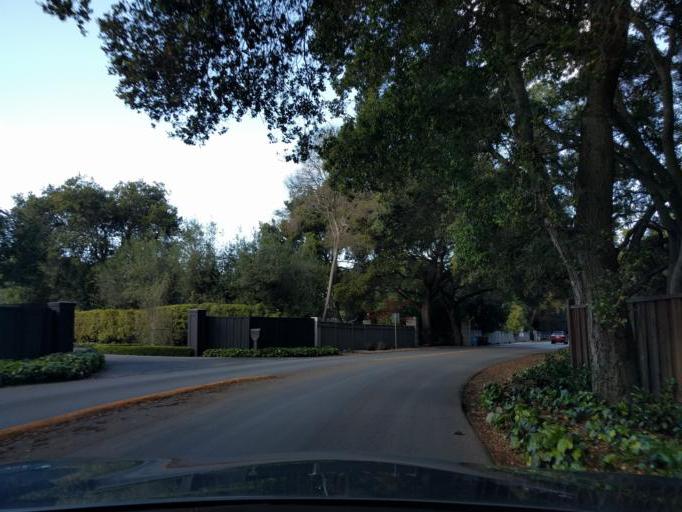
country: US
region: California
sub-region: San Mateo County
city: Atherton
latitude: 37.4592
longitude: -122.2027
